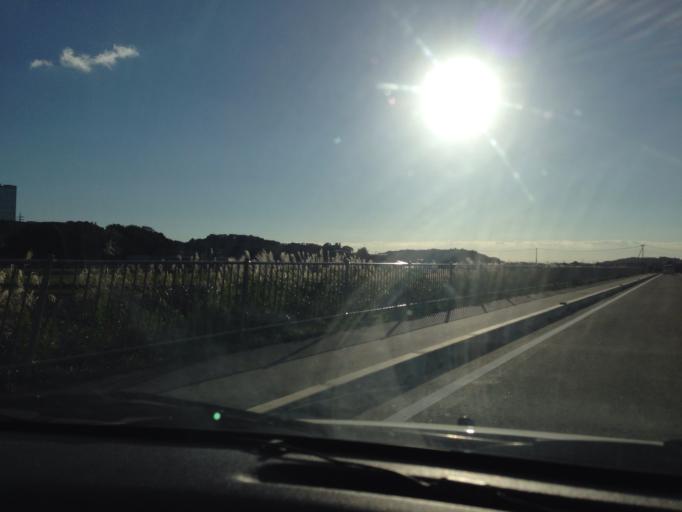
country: JP
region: Ibaraki
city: Inashiki
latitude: 36.0243
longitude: 140.3035
